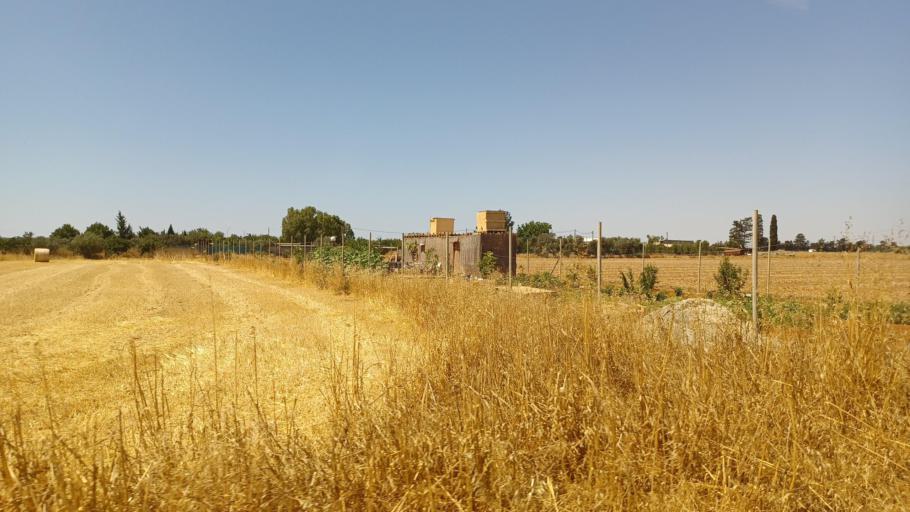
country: CY
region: Larnaka
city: Xylotymbou
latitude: 35.0276
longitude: 33.7343
